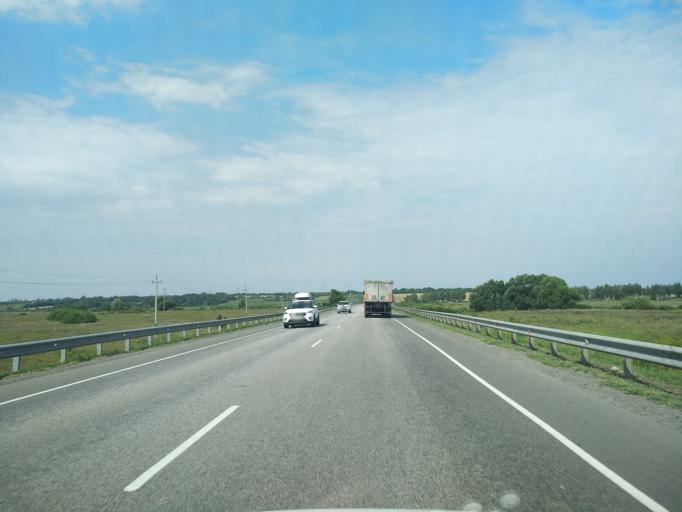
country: RU
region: Voronezj
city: Orlovo
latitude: 51.6757
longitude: 39.7408
